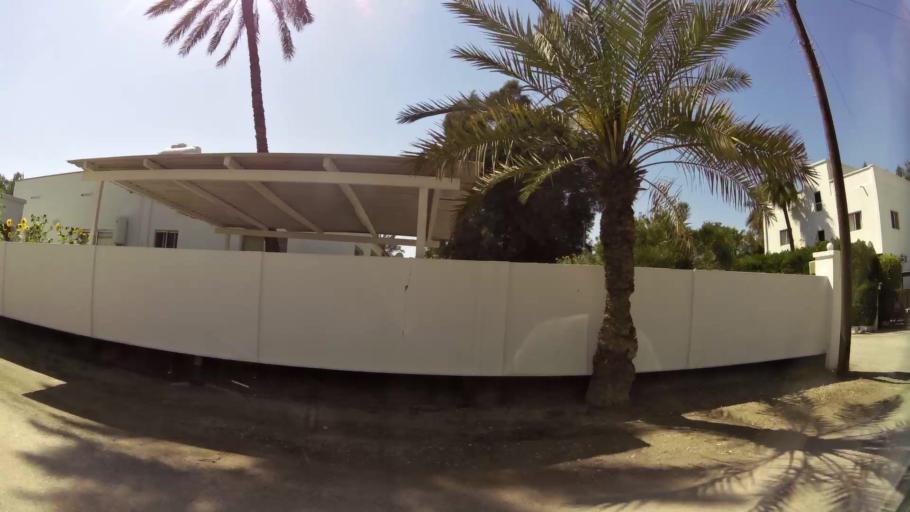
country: BH
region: Manama
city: Manama
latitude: 26.2164
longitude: 50.5841
